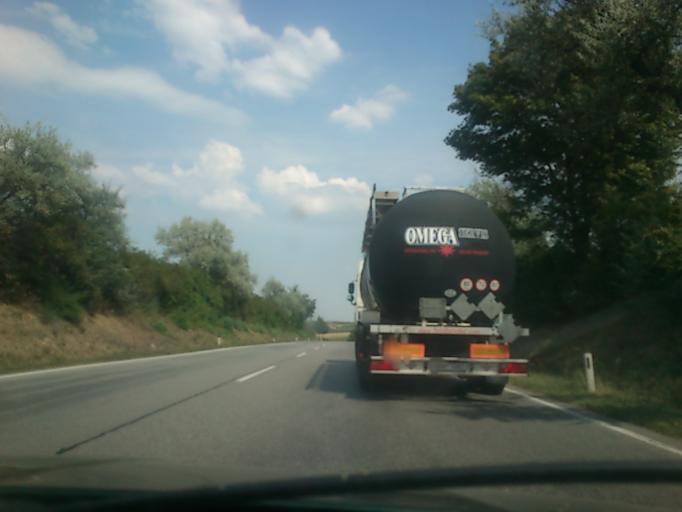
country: AT
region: Lower Austria
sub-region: Politischer Bezirk Mistelbach
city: Poysdorf
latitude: 48.6797
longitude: 16.6318
